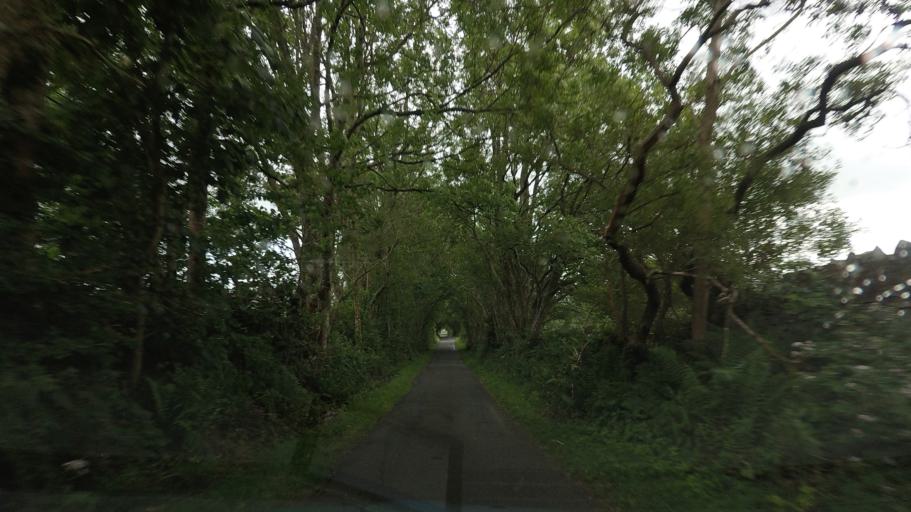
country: GB
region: Scotland
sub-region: Stirling
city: Killearn
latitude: 56.0795
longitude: -4.4498
